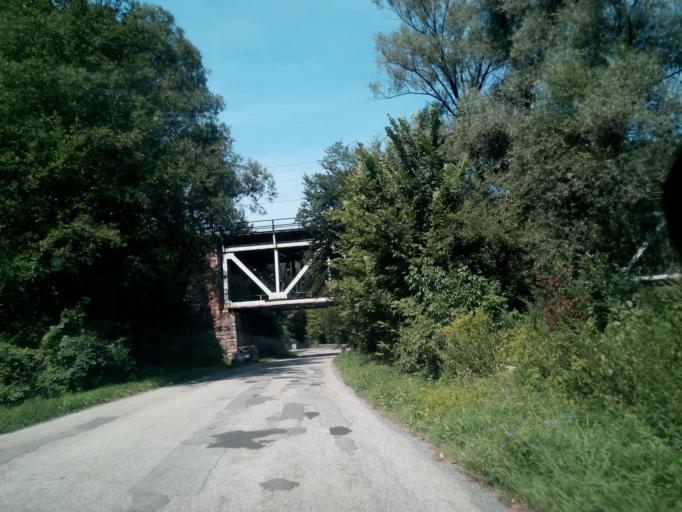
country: SK
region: Presovsky
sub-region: Okres Presov
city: Presov
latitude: 48.8567
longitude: 21.1929
